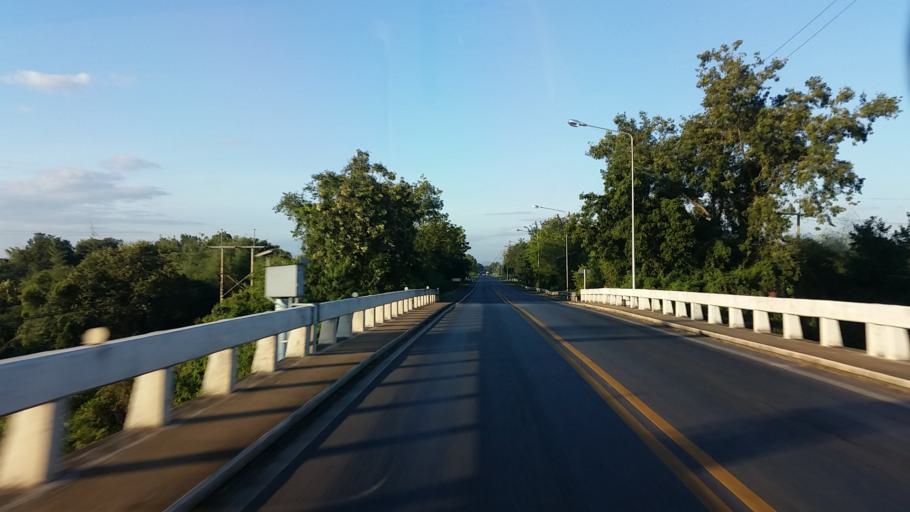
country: TH
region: Lop Buri
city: Chai Badan
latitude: 15.2640
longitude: 101.1929
